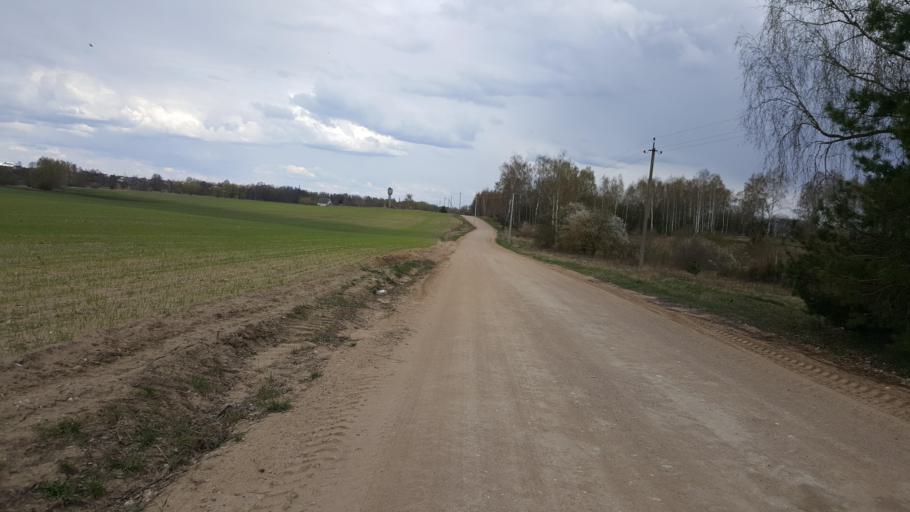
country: BY
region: Brest
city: Kamyanyets
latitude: 52.3964
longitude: 23.7444
